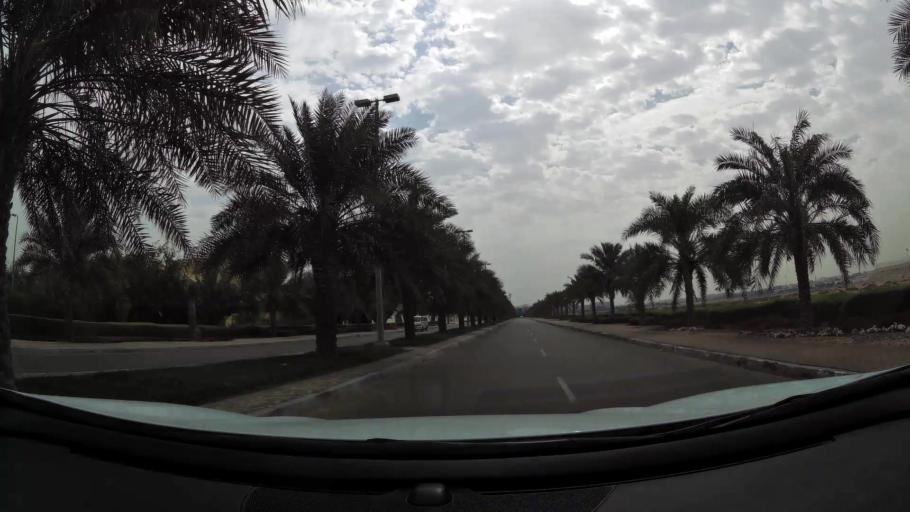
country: AE
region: Abu Dhabi
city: Abu Dhabi
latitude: 24.3183
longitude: 54.6132
